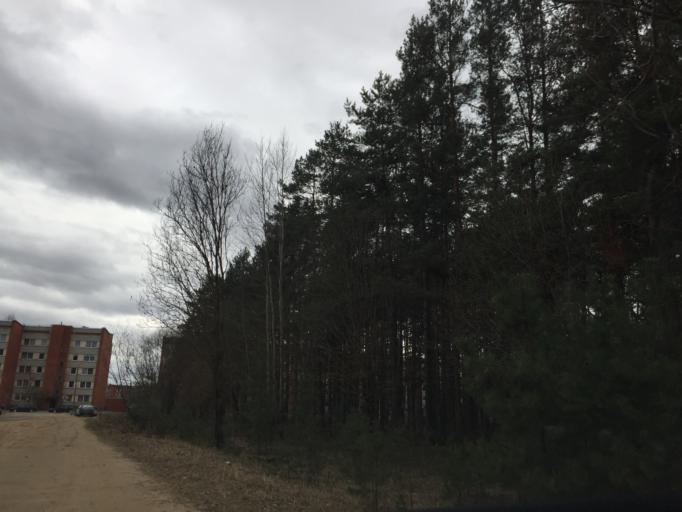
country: LV
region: Daugavpils
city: Daugavpils
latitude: 55.9062
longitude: 26.5371
